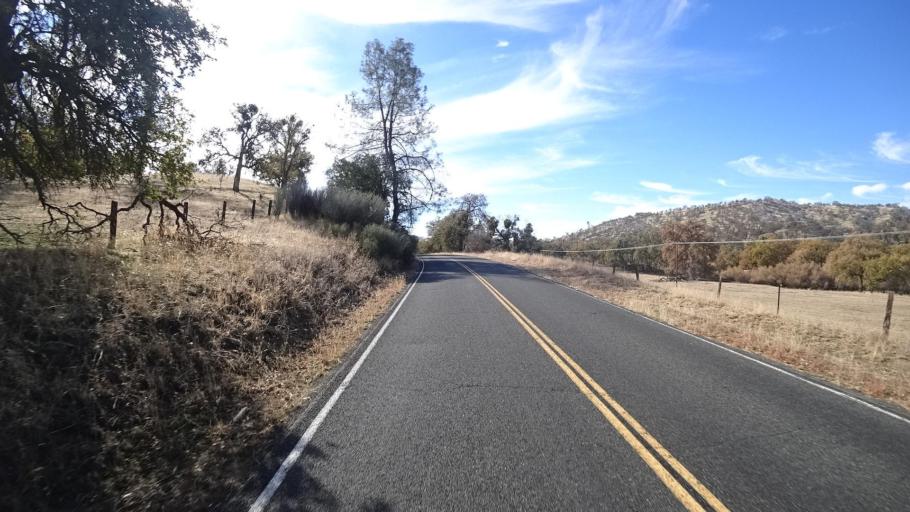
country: US
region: California
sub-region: Kern County
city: Alta Sierra
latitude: 35.6795
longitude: -118.7354
